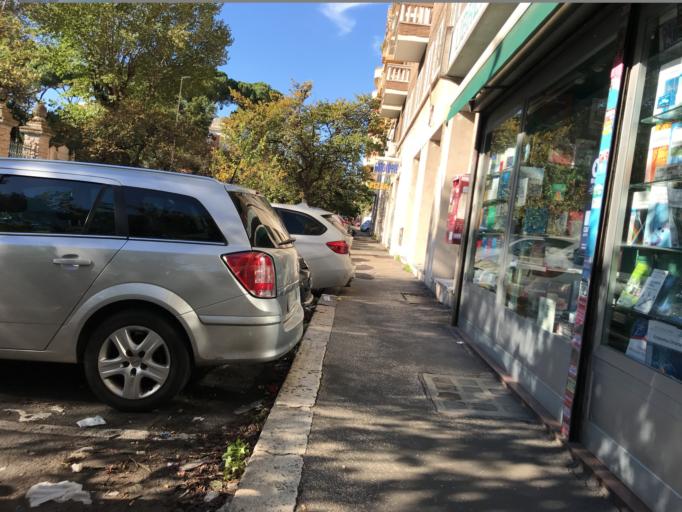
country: IT
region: Latium
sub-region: Citta metropolitana di Roma Capitale
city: Rome
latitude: 41.9065
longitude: 12.5165
